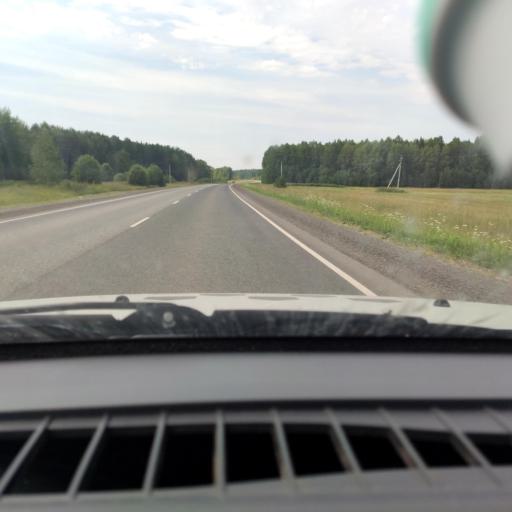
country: RU
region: Perm
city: Siva
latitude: 58.4882
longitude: 54.0614
